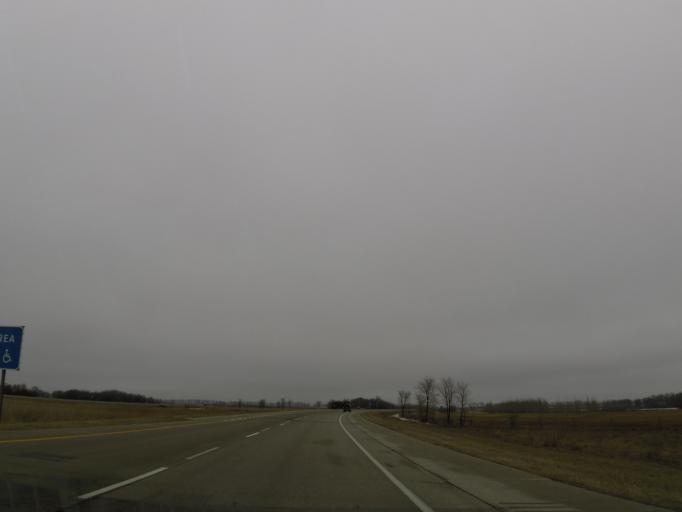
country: US
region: North Dakota
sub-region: Walsh County
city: Grafton
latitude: 48.4534
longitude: -97.1945
